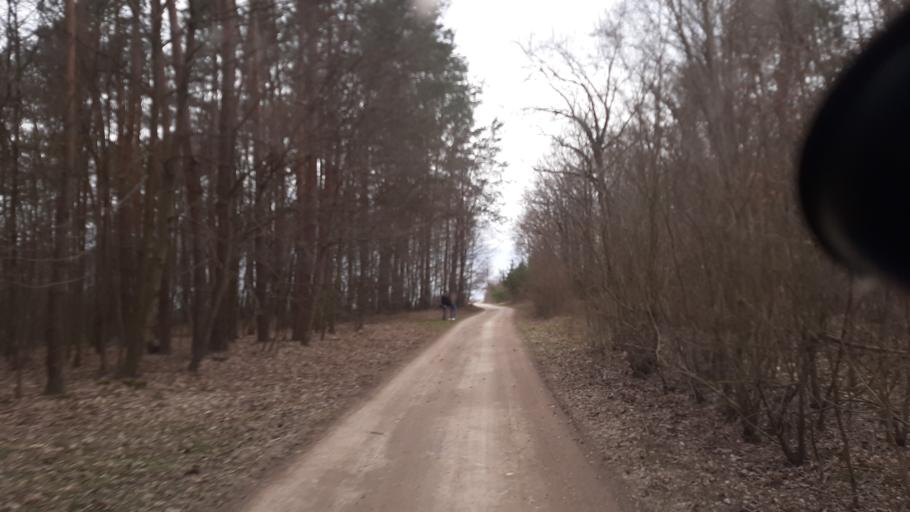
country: PL
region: Lublin Voivodeship
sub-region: Powiat lubartowski
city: Abramow
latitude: 51.4455
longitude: 22.3382
